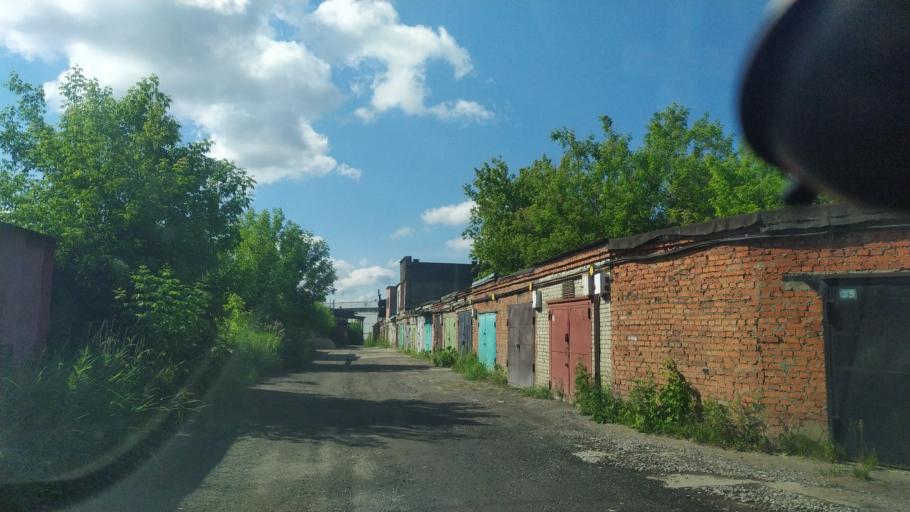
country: RU
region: Moscow
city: Vostochnyy
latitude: 55.8127
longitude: 37.8664
